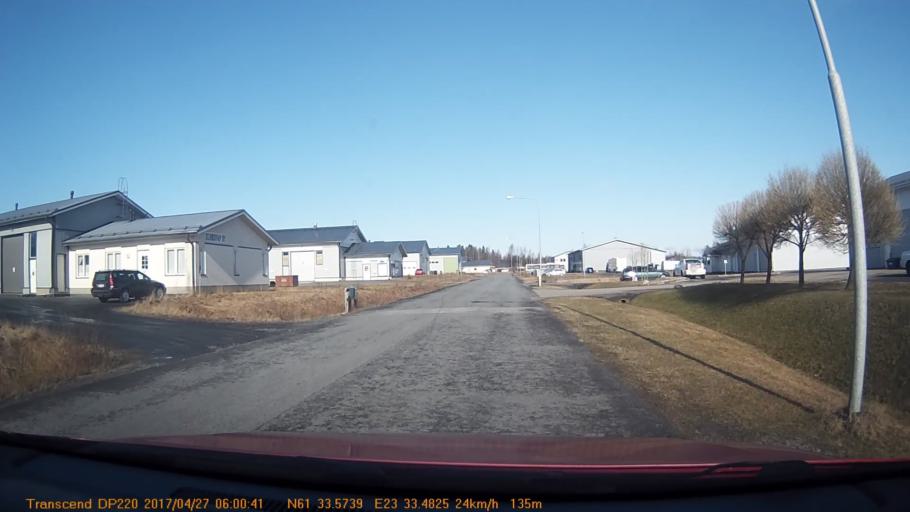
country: FI
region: Pirkanmaa
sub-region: Tampere
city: Yloejaervi
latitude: 61.5595
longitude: 23.5582
